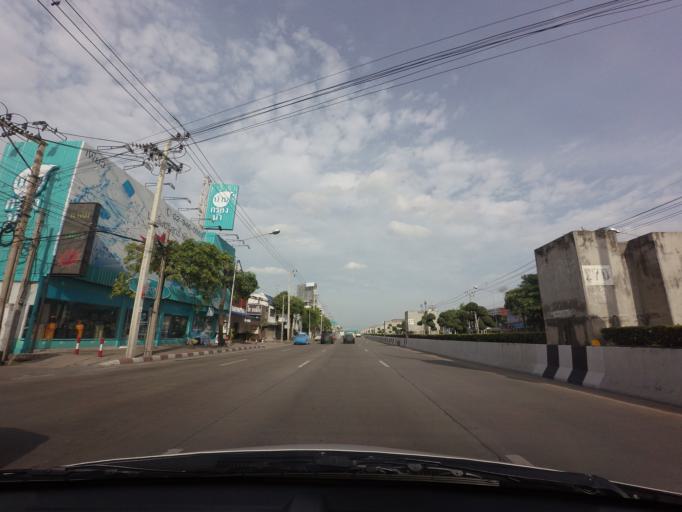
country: TH
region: Bangkok
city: Khan Na Yao
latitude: 13.8131
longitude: 100.6461
